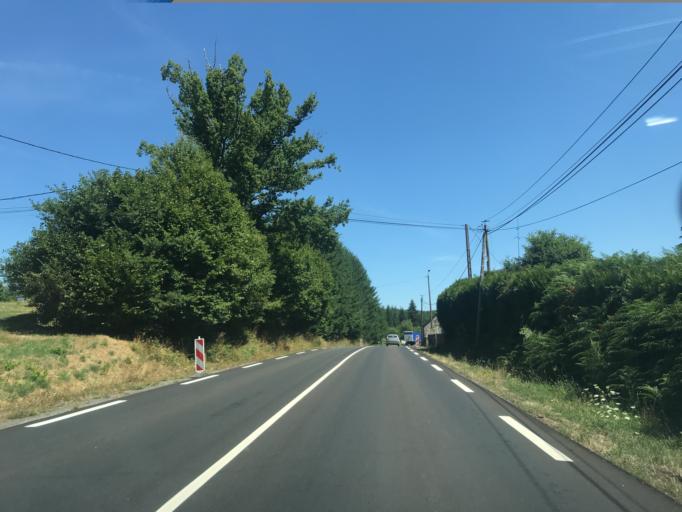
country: FR
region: Limousin
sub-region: Departement de la Correze
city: Egletons
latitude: 45.3838
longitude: 2.0182
